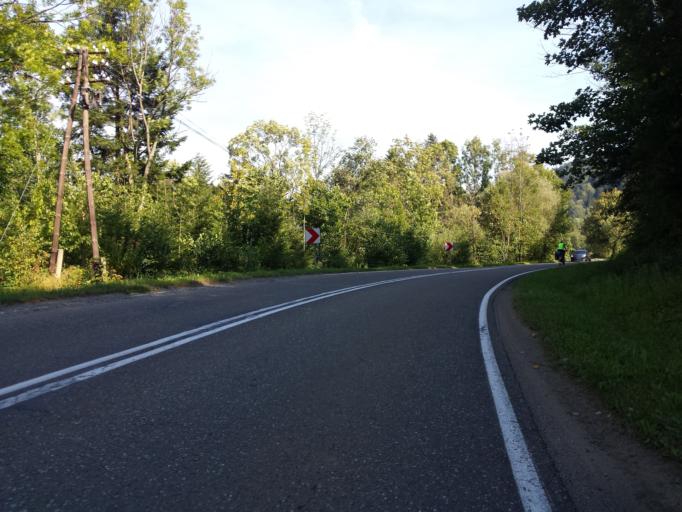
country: PL
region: Subcarpathian Voivodeship
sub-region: Powiat leski
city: Baligrod
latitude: 49.3071
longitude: 22.2763
